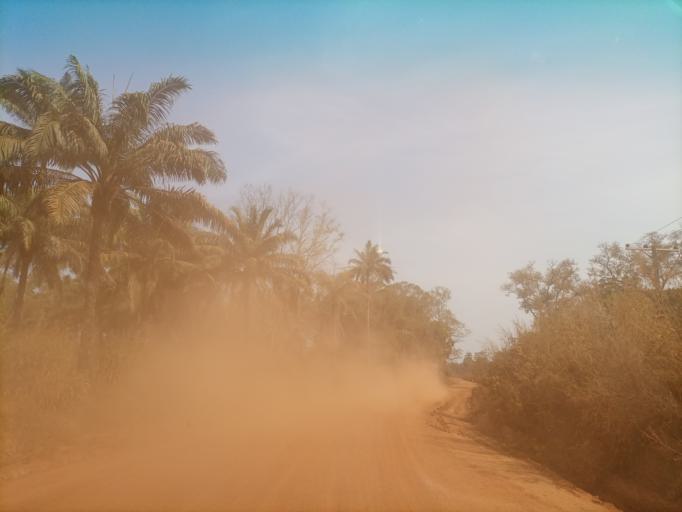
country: NG
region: Enugu
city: Eha Amufu
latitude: 6.6681
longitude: 7.7519
